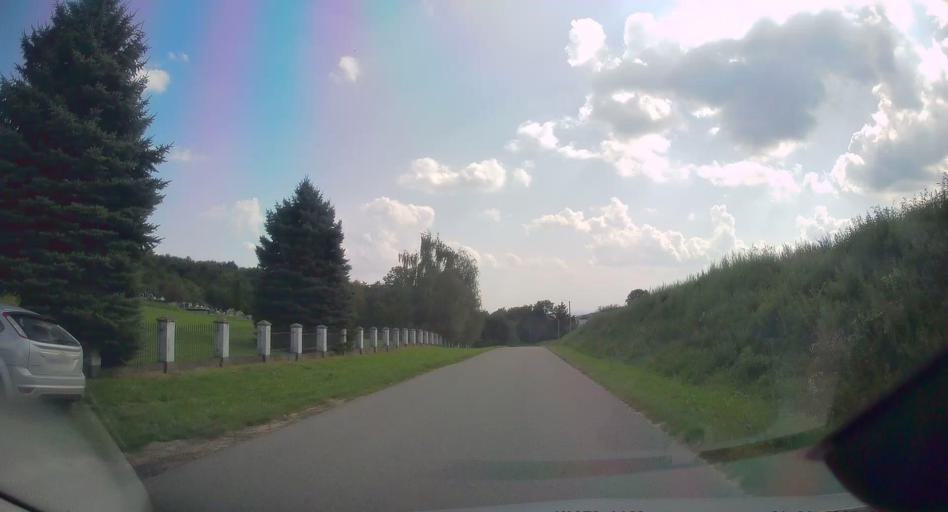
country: PL
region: Lesser Poland Voivodeship
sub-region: Powiat bochenski
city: Dziewin
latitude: 50.1530
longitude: 20.4636
